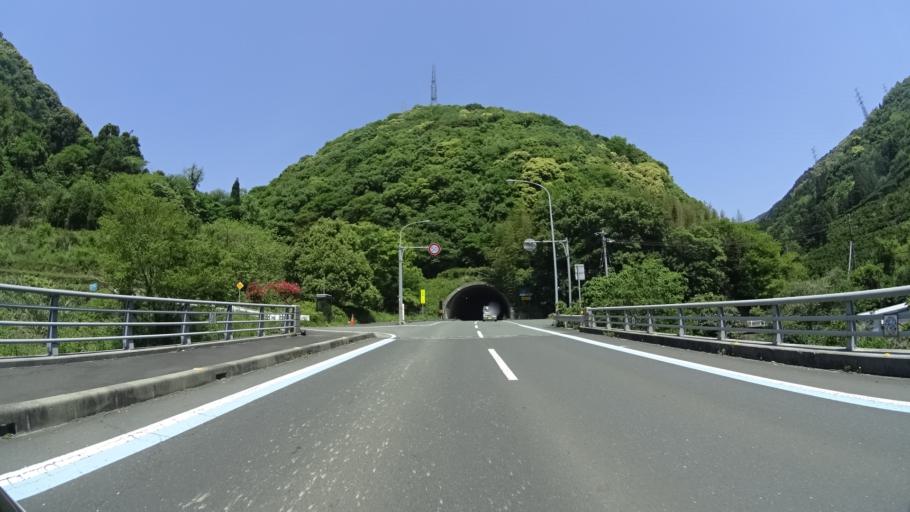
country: JP
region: Ehime
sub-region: Nishiuwa-gun
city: Ikata-cho
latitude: 33.5078
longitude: 132.3967
